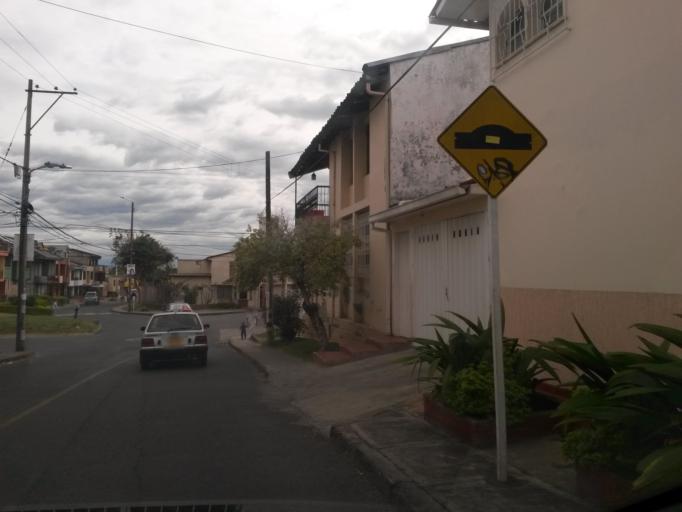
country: CO
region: Cauca
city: Popayan
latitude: 2.4532
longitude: -76.6056
